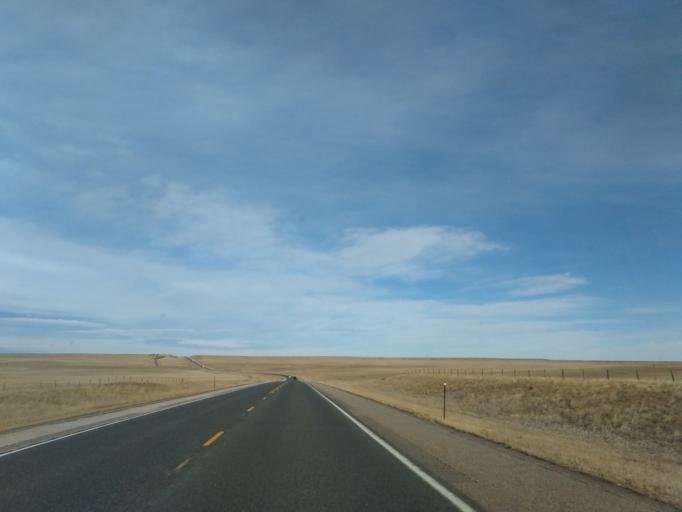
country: US
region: Wyoming
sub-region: Laramie County
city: Pine Bluffs
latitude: 41.5721
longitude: -104.2770
